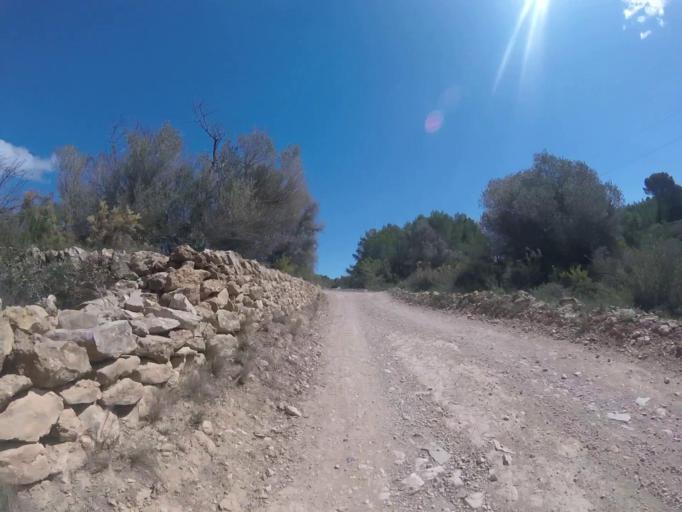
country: ES
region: Valencia
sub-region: Provincia de Castello
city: Santa Magdalena de Pulpis
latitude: 40.3249
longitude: 0.3513
